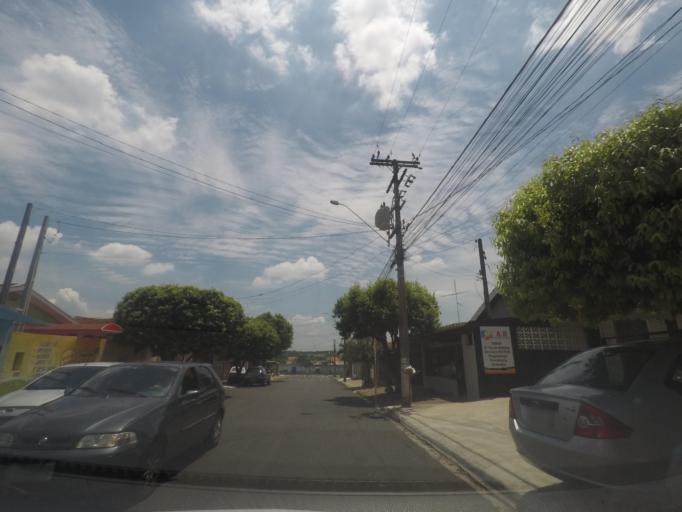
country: BR
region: Sao Paulo
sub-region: Nova Odessa
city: Nova Odessa
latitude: -22.7974
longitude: -47.2787
